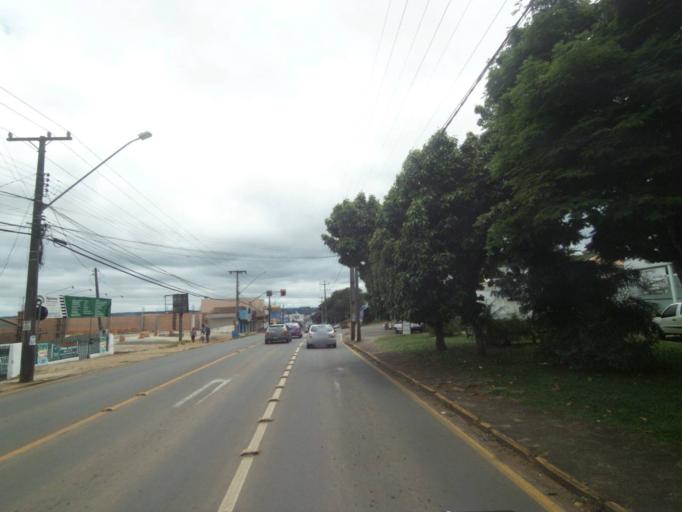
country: BR
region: Parana
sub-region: Telemaco Borba
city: Telemaco Borba
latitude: -24.3324
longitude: -50.6352
